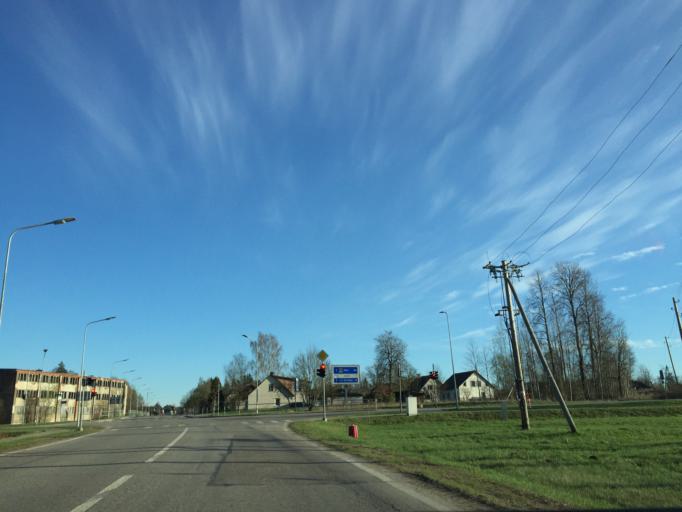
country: LV
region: Valkas Rajons
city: Valka
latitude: 57.7808
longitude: 25.9914
